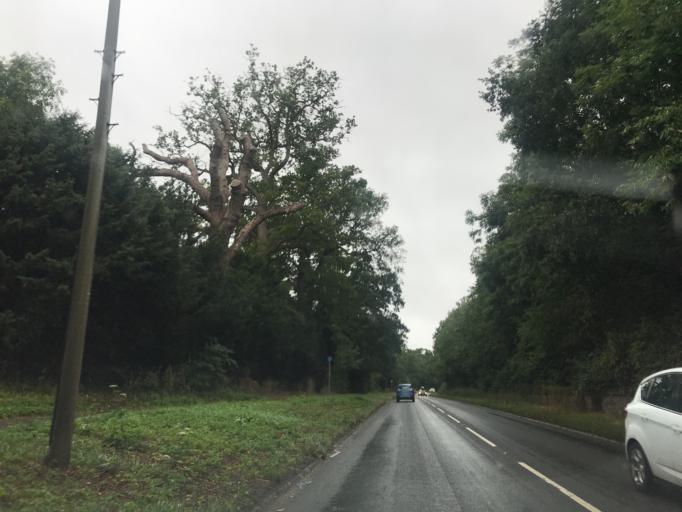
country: GB
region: England
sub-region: Buckinghamshire
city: Aylesbury
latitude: 51.8057
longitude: -0.8376
